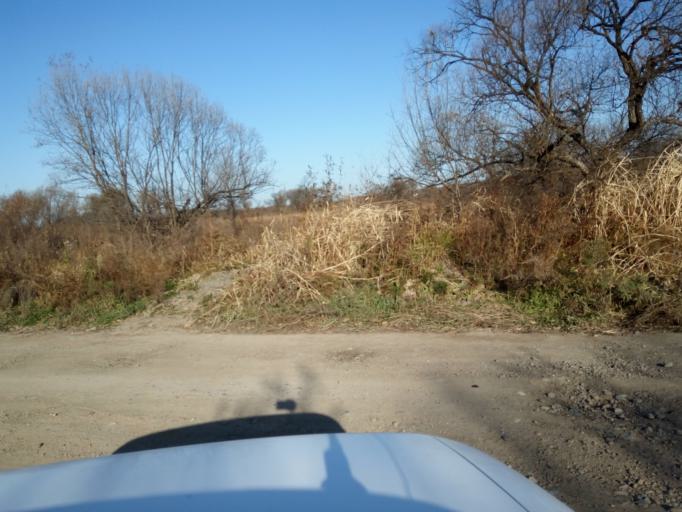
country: RU
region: Primorskiy
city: Lazo
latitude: 45.8783
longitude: 133.6375
